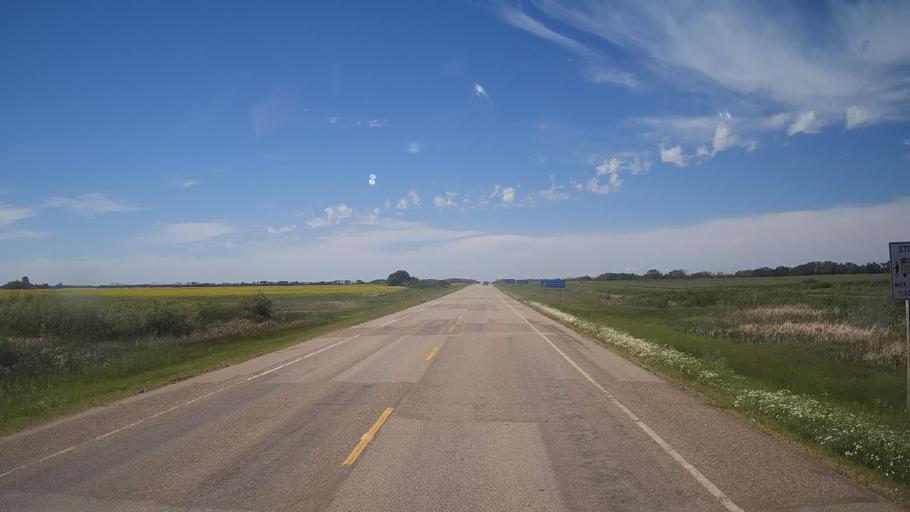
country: CA
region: Saskatchewan
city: Langenburg
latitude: 50.7795
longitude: -101.5156
